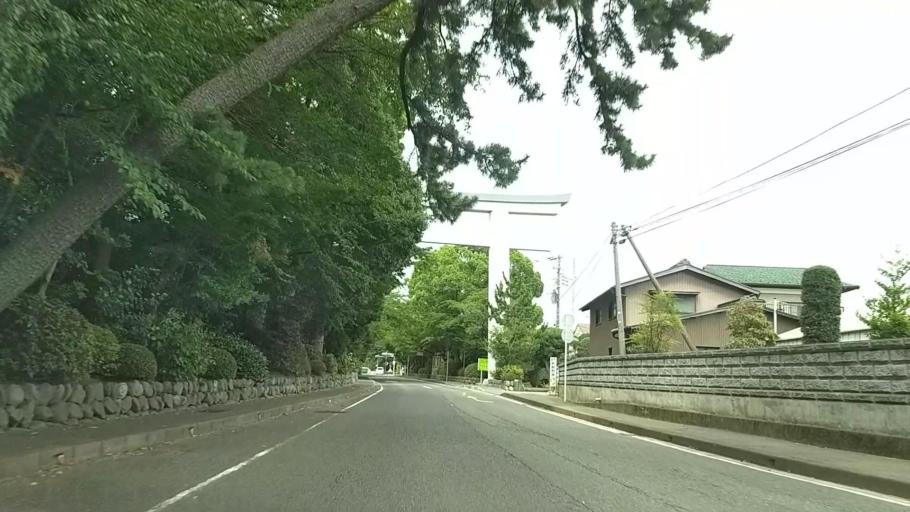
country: JP
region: Kanagawa
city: Chigasaki
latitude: 35.3754
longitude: 139.3807
